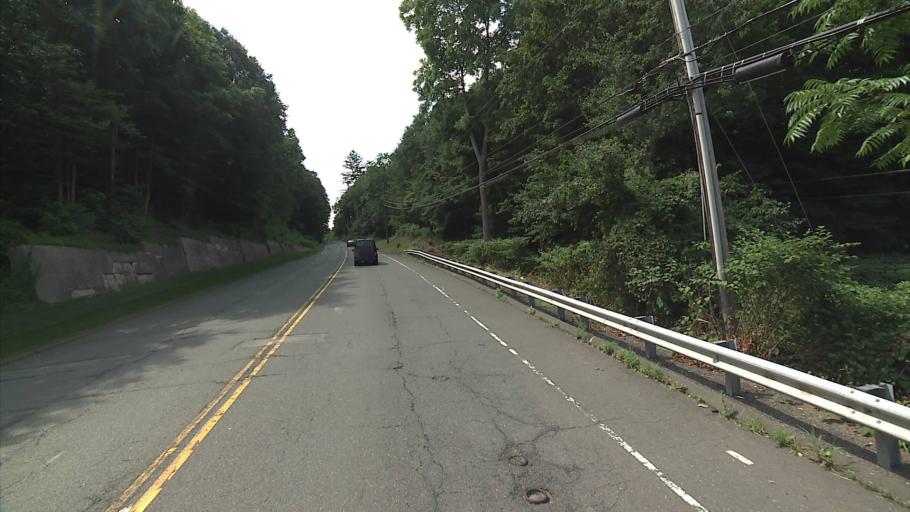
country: US
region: Connecticut
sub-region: Hartford County
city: Glastonbury Center
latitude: 41.6628
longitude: -72.6046
